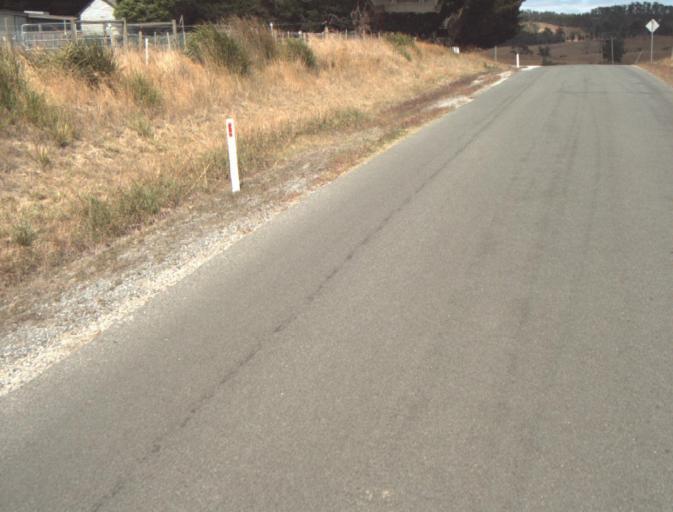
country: AU
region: Tasmania
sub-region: Launceston
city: Mayfield
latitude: -41.2082
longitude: 147.1177
